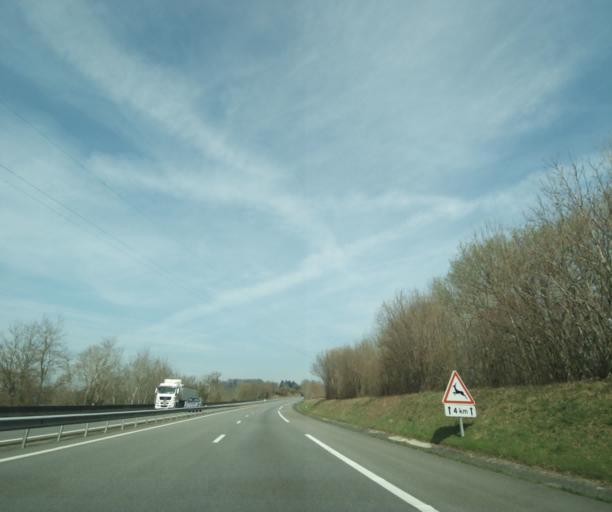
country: FR
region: Limousin
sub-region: Departement de la Correze
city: Uzerche
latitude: 45.5029
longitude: 1.5152
